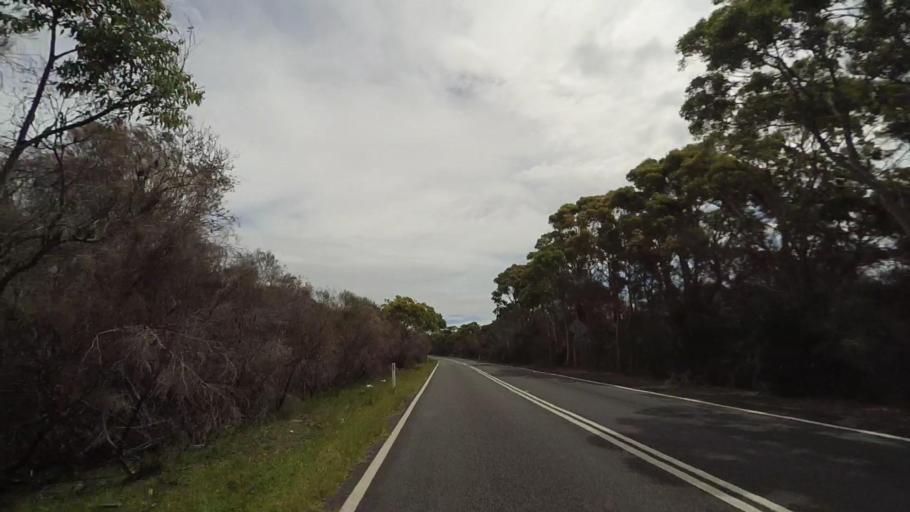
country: AU
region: New South Wales
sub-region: Sutherland Shire
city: Bundeena
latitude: -34.0885
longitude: 151.1372
